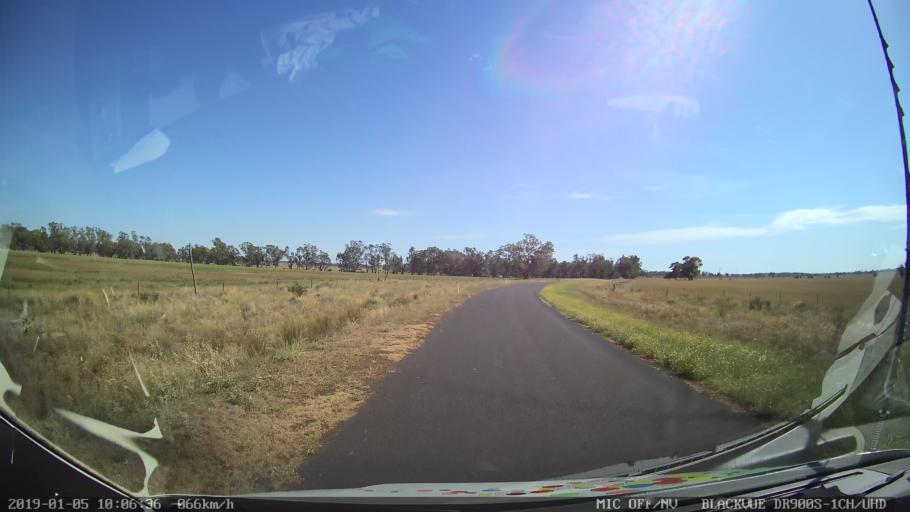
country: AU
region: New South Wales
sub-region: Gilgandra
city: Gilgandra
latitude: -31.6566
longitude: 148.8701
